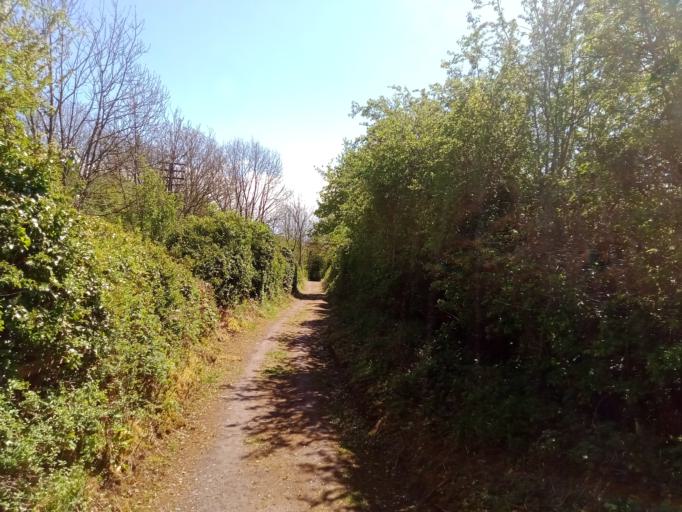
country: IE
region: Leinster
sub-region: Kilkenny
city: Kilkenny
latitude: 52.6911
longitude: -7.2620
